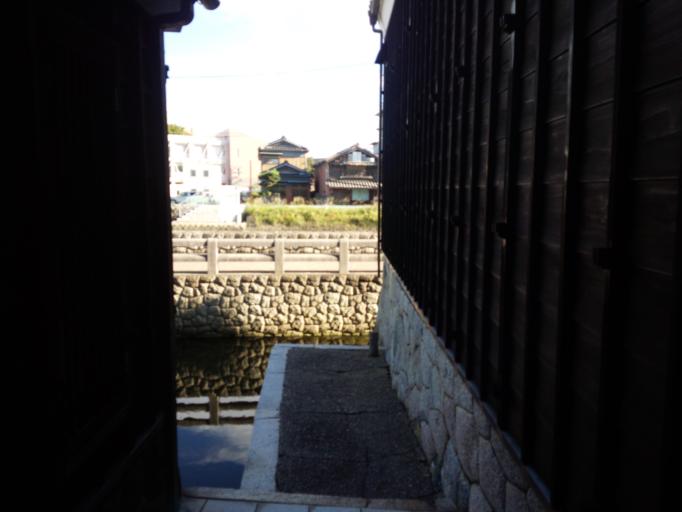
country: JP
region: Mie
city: Ise
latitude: 34.4965
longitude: 136.7177
